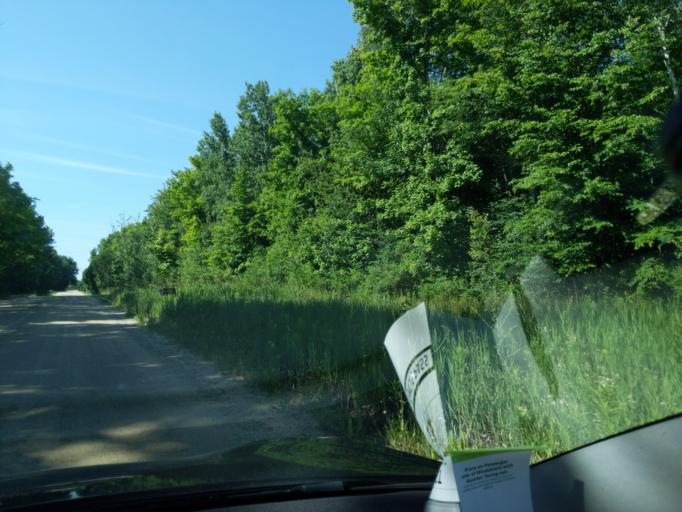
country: US
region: Michigan
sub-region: Cheboygan County
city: Cheboygan
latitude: 45.6730
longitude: -84.6508
